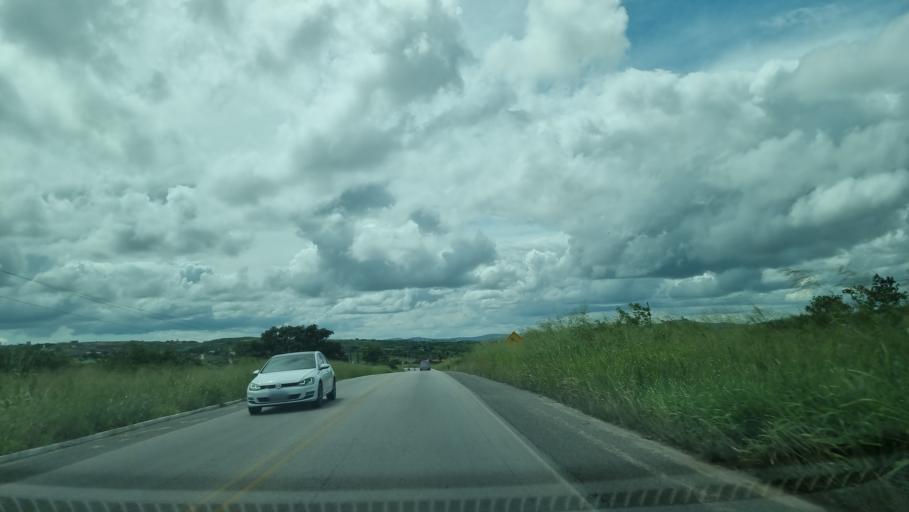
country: BR
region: Pernambuco
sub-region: Caruaru
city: Caruaru
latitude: -8.3388
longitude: -35.9815
